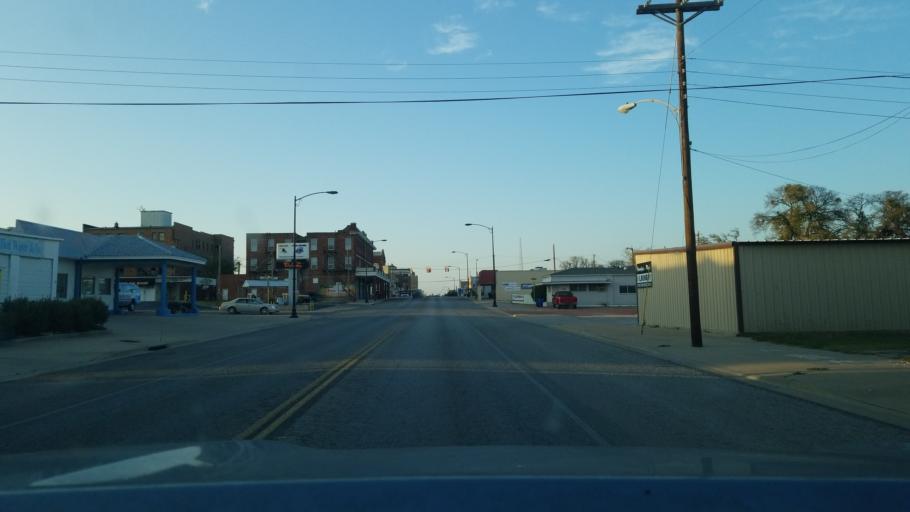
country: US
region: Texas
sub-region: Eastland County
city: Cisco
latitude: 32.3868
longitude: -98.9784
